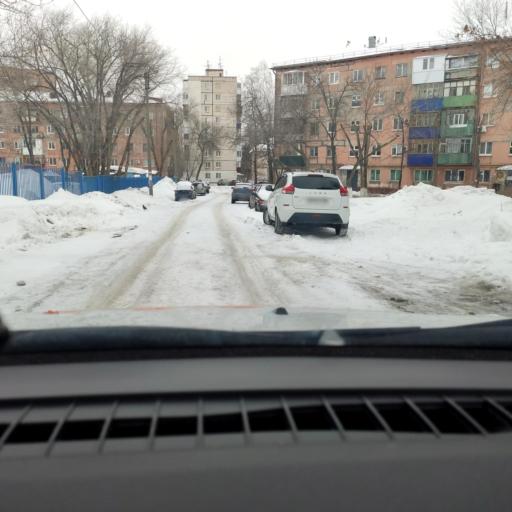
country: RU
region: Samara
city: Novokuybyshevsk
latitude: 53.0926
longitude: 49.9694
